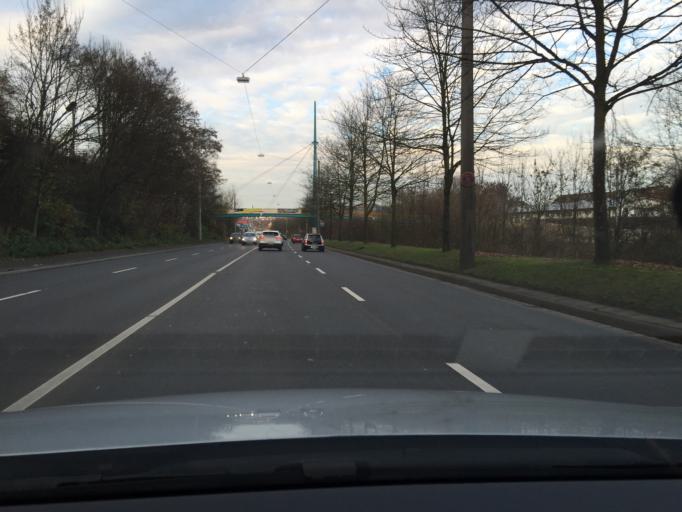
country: DE
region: North Rhine-Westphalia
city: Herdecke
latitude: 51.3799
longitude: 7.4505
